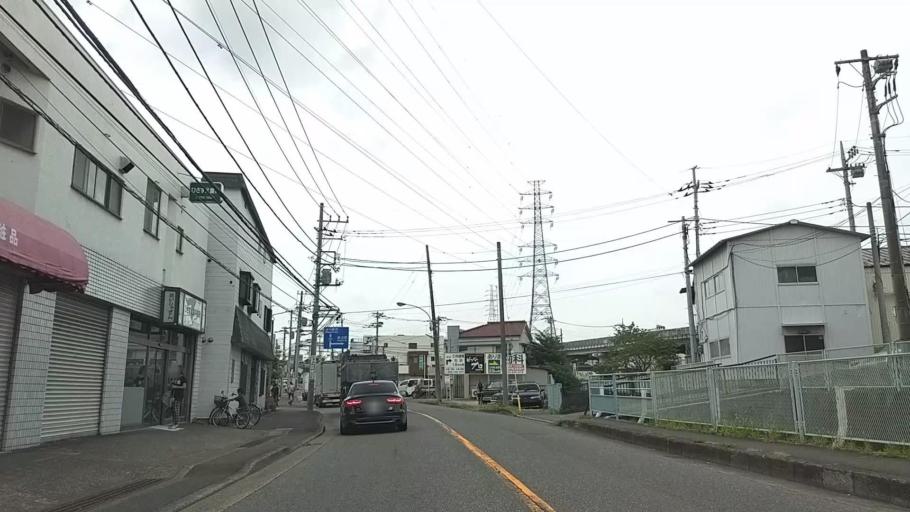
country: JP
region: Tokyo
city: Chofugaoka
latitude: 35.5655
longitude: 139.6126
